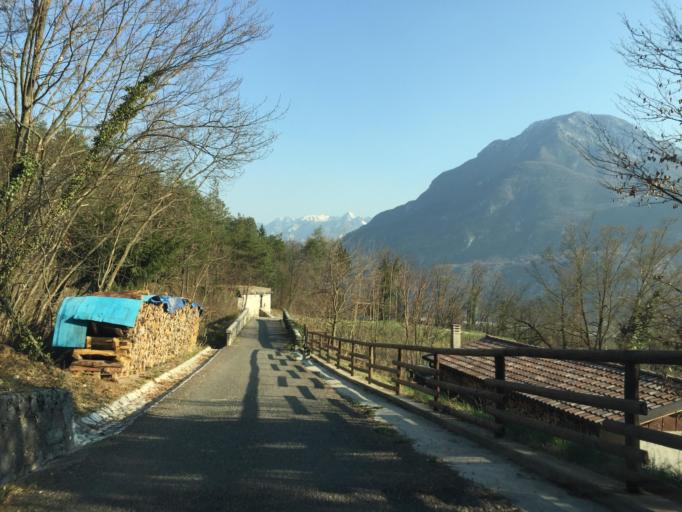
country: IT
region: Friuli Venezia Giulia
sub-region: Provincia di Udine
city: Amaro
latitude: 46.3787
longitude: 13.0912
